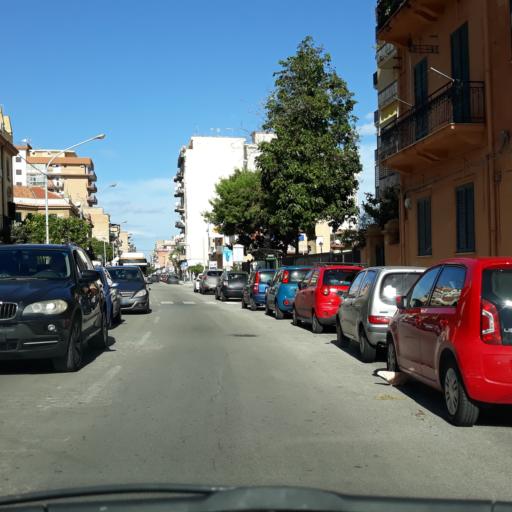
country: IT
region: Sicily
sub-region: Palermo
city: Palermo
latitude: 38.1484
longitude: 13.3708
